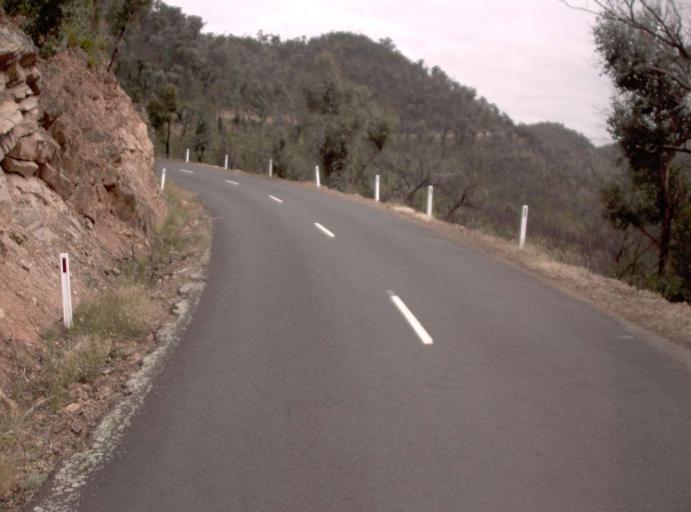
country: AU
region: Victoria
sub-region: Wellington
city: Heyfield
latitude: -37.7282
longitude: 146.6696
